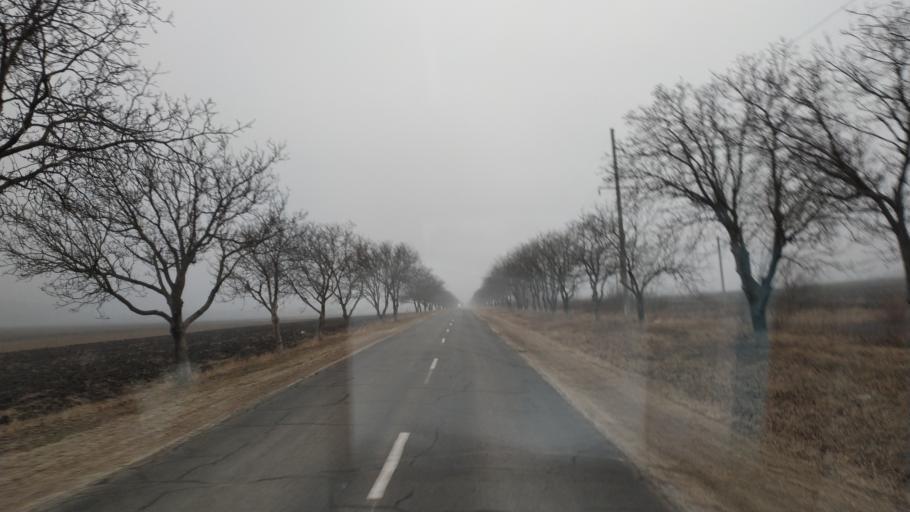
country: MD
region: Laloveni
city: Ialoveni
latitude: 46.9335
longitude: 28.8093
